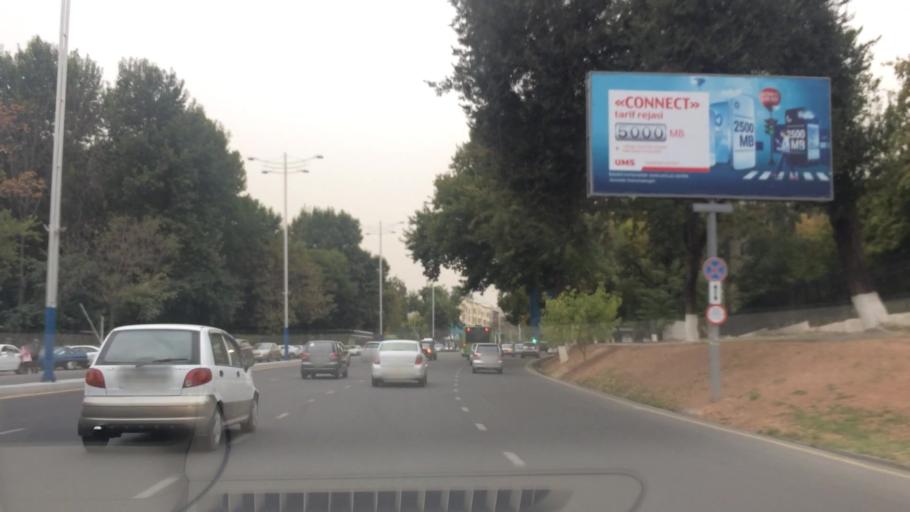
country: UZ
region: Toshkent Shahri
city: Tashkent
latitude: 41.3071
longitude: 69.2951
